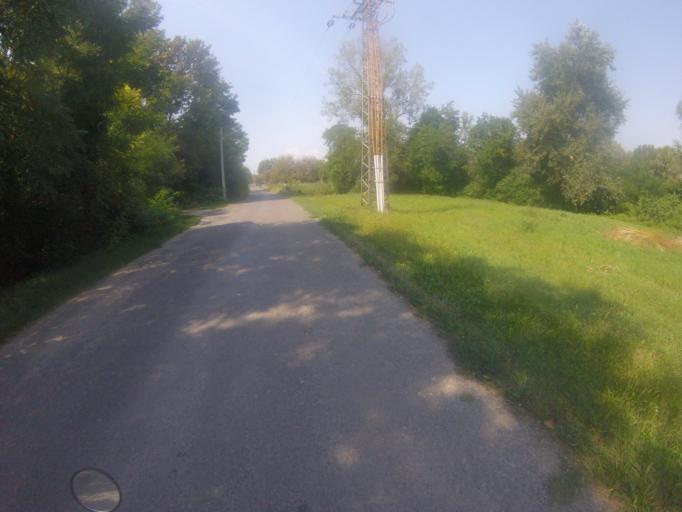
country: HU
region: Bacs-Kiskun
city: Ersekcsanad
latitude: 46.2575
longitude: 18.9221
